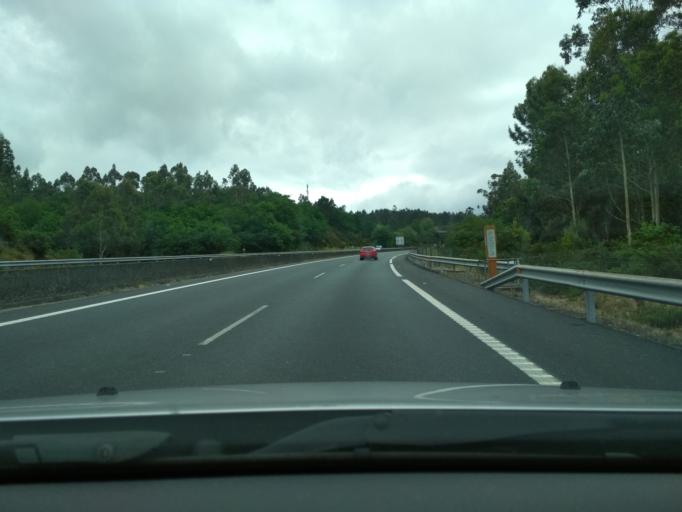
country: ES
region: Galicia
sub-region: Provincia da Coruna
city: Santiago de Compostela
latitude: 42.8421
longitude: -8.5714
